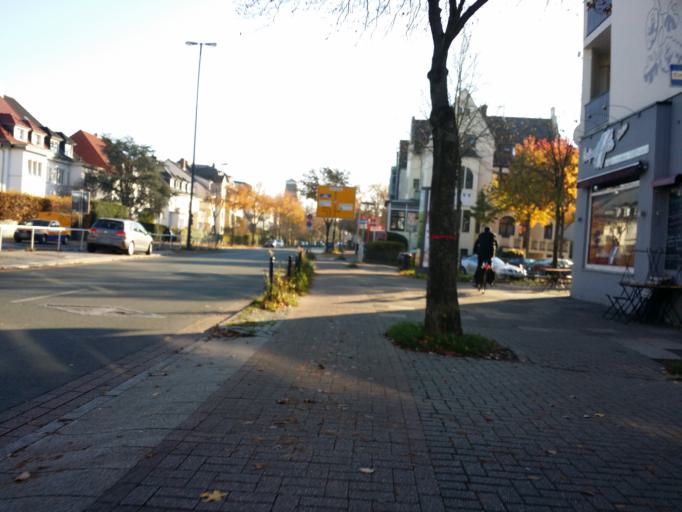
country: DE
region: Bremen
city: Bremen
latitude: 53.0830
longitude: 8.8273
